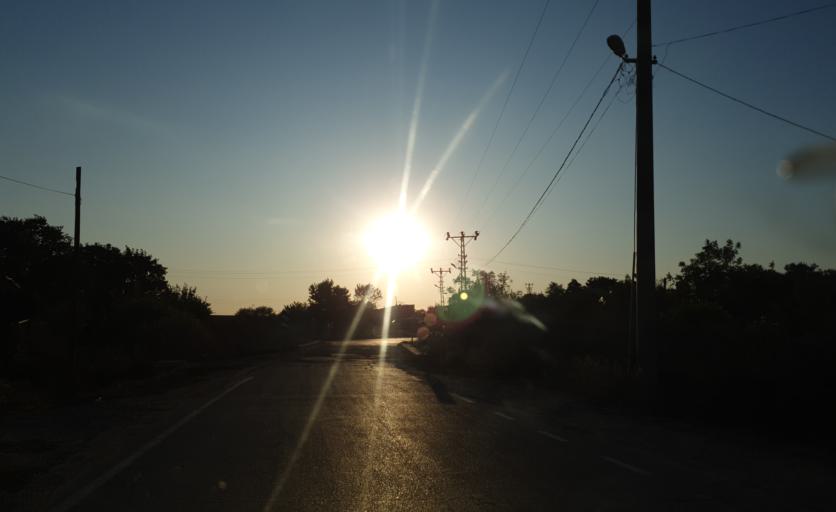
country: TR
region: Tekirdag
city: Beyazkoy
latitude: 41.3358
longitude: 27.7392
